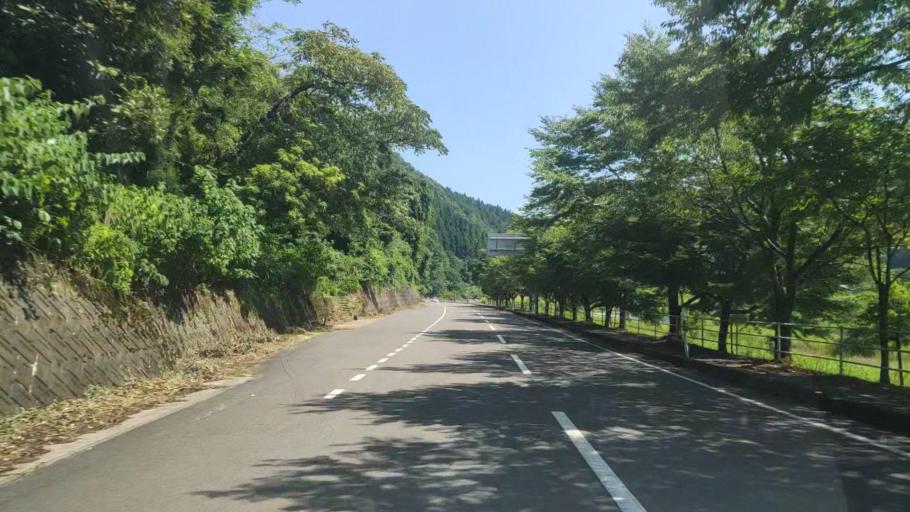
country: JP
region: Gifu
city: Godo
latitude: 35.6037
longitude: 136.6284
